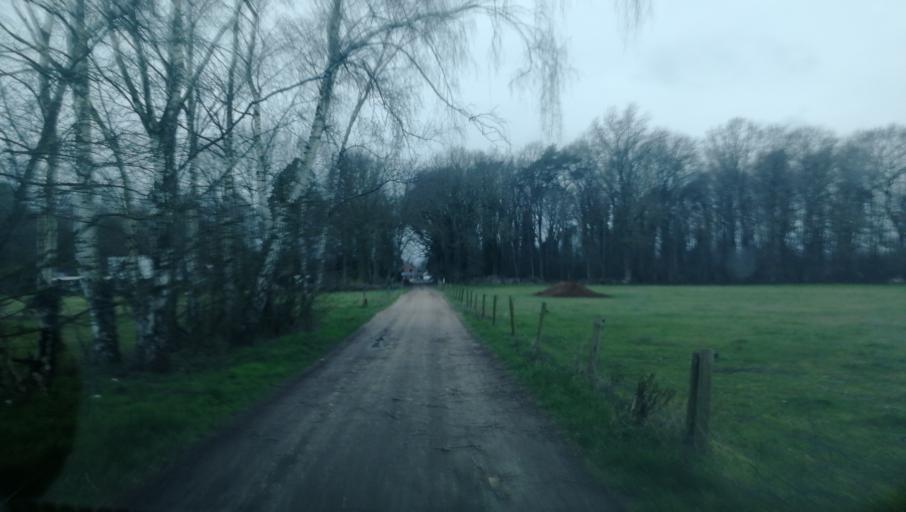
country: NL
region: Limburg
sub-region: Gemeente Venlo
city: Venlo
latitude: 51.4059
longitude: 6.1731
